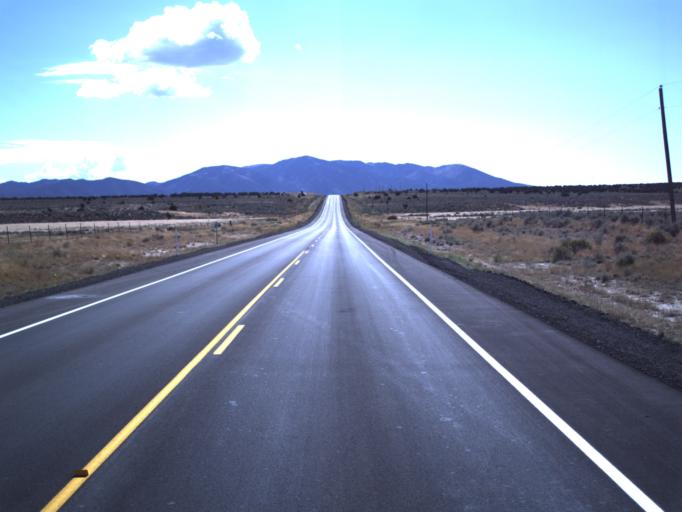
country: US
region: Utah
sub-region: Utah County
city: Eagle Mountain
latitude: 40.0741
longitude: -112.3385
